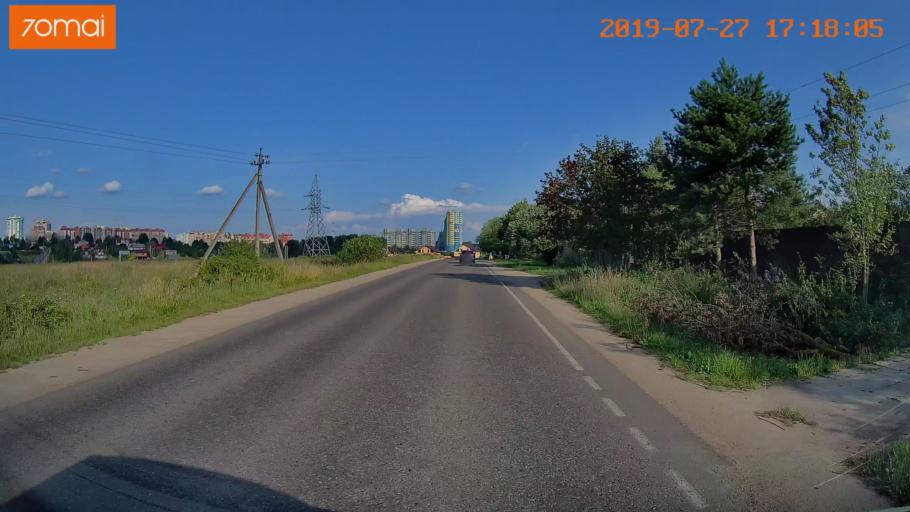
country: RU
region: Ivanovo
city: Novo-Talitsy
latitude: 57.0328
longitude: 40.9025
